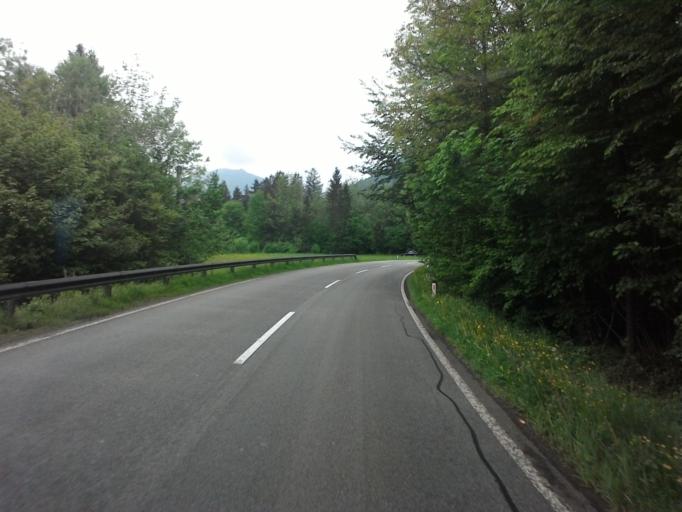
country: AT
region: Styria
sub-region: Politischer Bezirk Liezen
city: Altenmarkt bei Sankt Gallen
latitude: 47.7129
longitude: 14.6806
